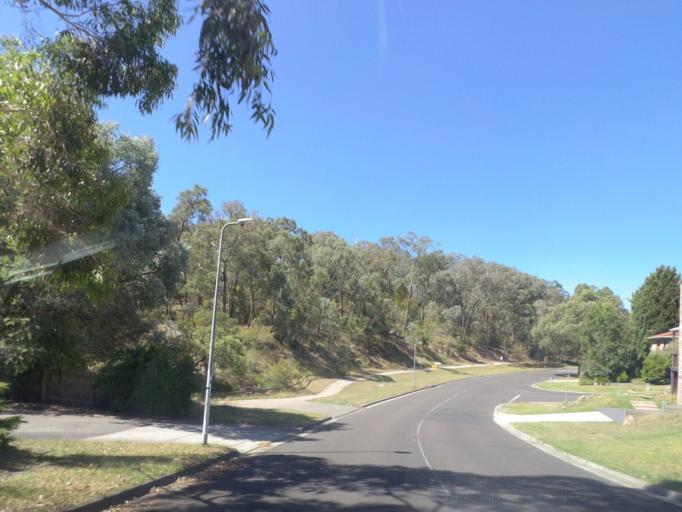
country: AU
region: Victoria
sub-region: Manningham
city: Park Orchards
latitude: -37.7970
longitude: 145.2182
